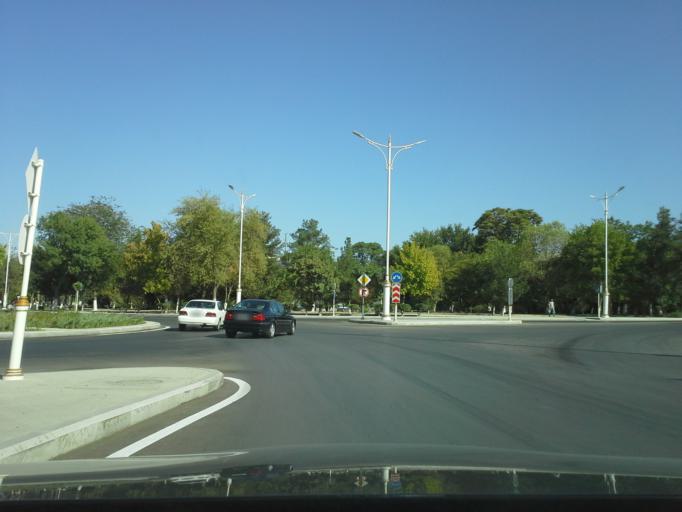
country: TM
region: Ahal
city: Ashgabat
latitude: 37.9581
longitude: 58.3451
